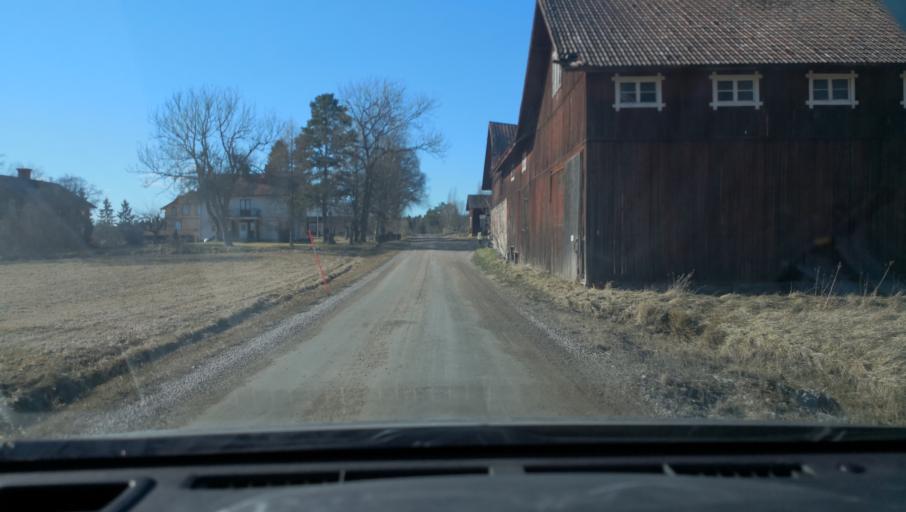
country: SE
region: Vaestmanland
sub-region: Sala Kommun
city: Sala
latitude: 60.1522
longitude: 16.6362
